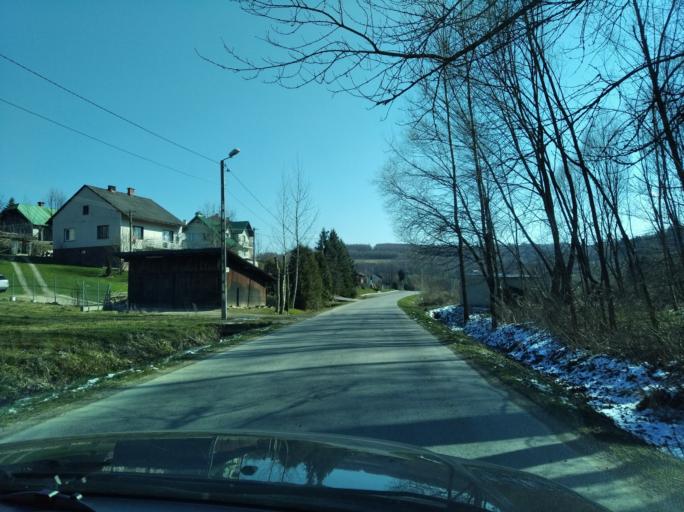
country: PL
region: Subcarpathian Voivodeship
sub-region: Powiat strzyzowski
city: Jawornik
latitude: 49.8455
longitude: 21.8881
